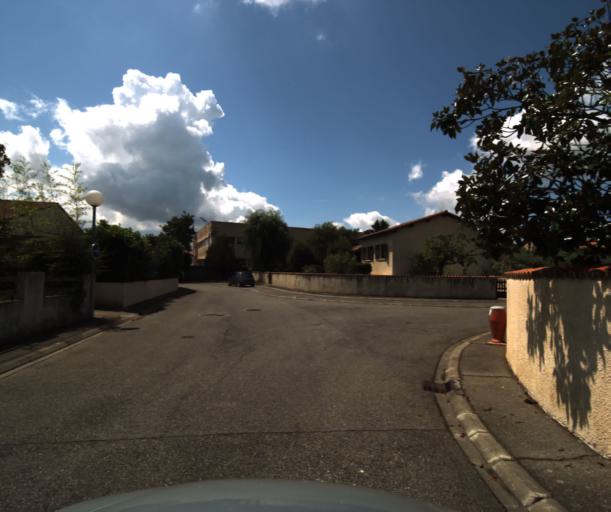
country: FR
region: Midi-Pyrenees
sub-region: Departement de la Haute-Garonne
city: Pinsaguel
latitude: 43.5170
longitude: 1.3891
